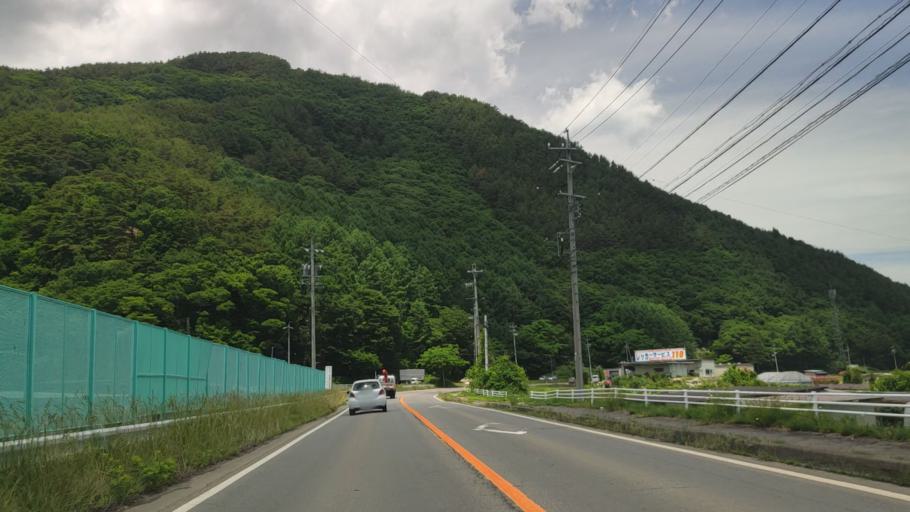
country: JP
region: Nagano
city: Kamimaruko
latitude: 36.2528
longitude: 138.2614
